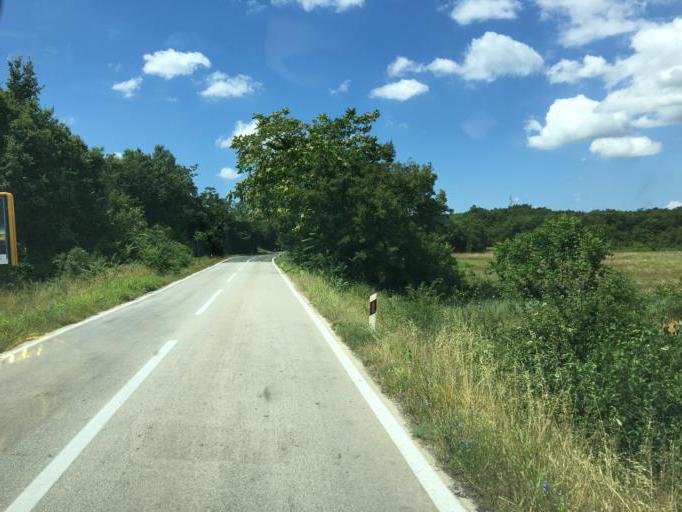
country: HR
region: Istarska
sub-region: Grad Rovinj
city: Rovinj
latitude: 45.1464
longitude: 13.7329
